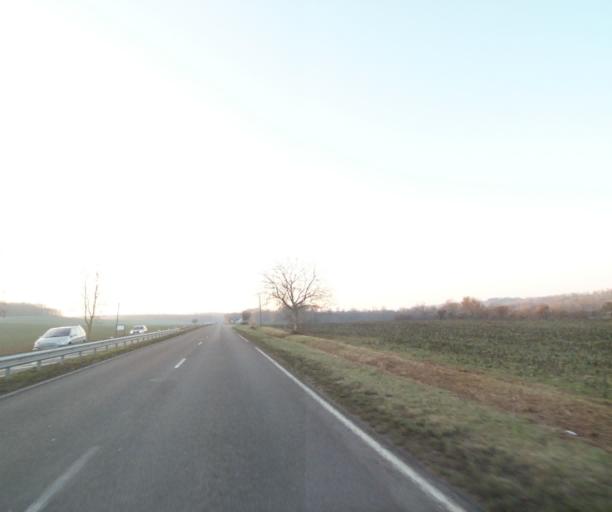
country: FR
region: Lorraine
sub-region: Departement de la Meuse
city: Ancerville
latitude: 48.6070
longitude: 5.0207
